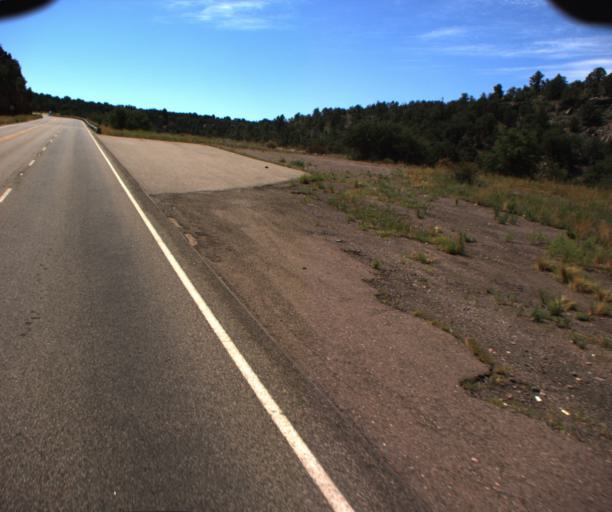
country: US
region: Arizona
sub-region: Navajo County
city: Cibecue
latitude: 33.7365
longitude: -110.5273
